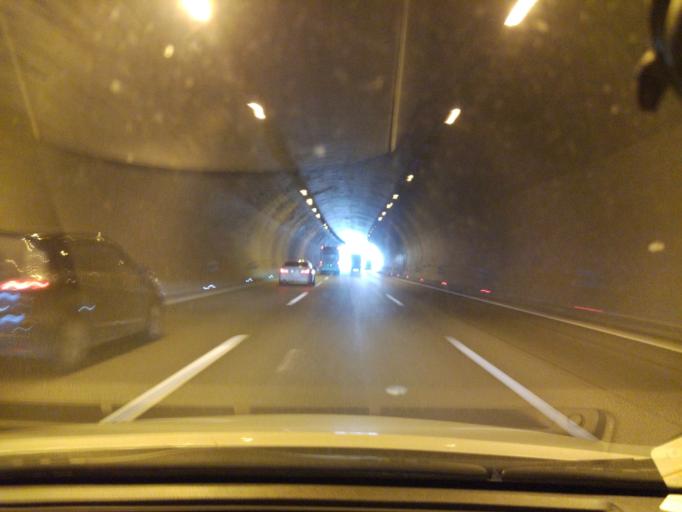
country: TR
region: Kocaeli
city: Hereke
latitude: 40.7849
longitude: 29.6095
